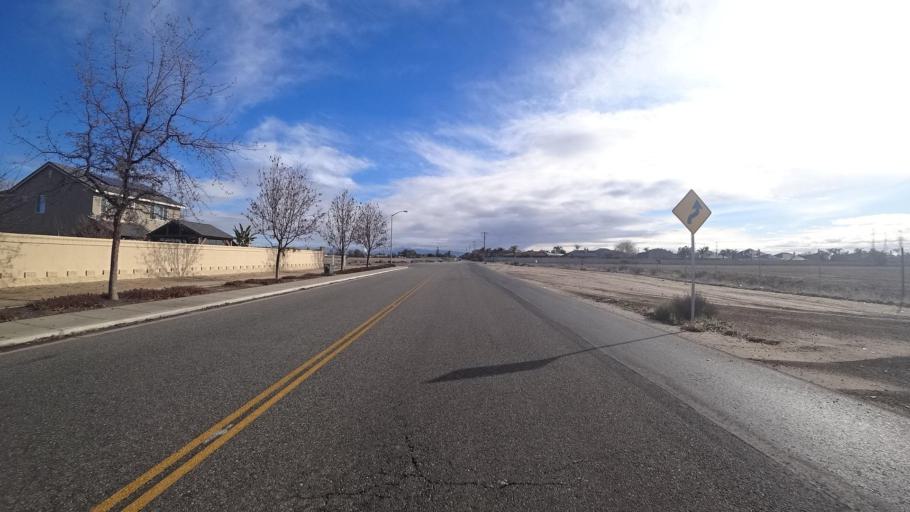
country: US
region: California
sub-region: Kern County
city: Rosedale
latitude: 35.3909
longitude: -119.1735
